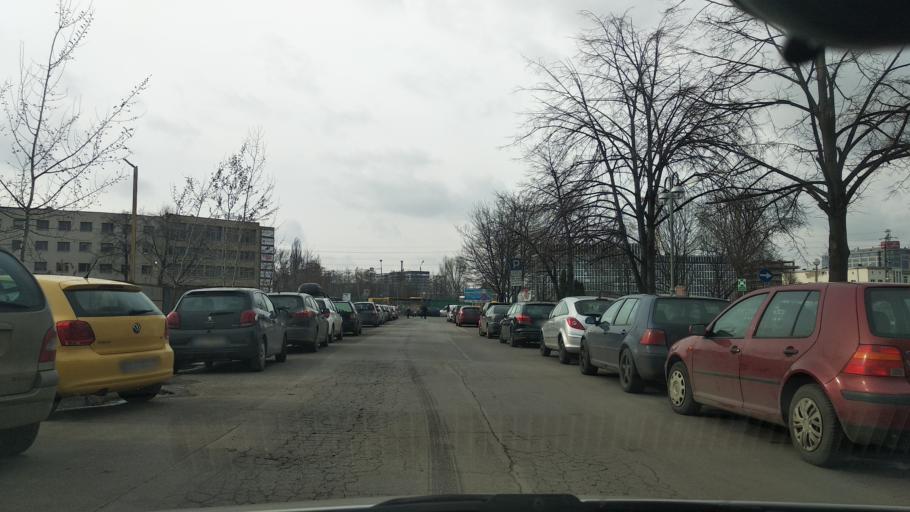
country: PL
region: Silesian Voivodeship
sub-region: Katowice
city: Katowice
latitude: 50.2636
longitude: 19.0128
